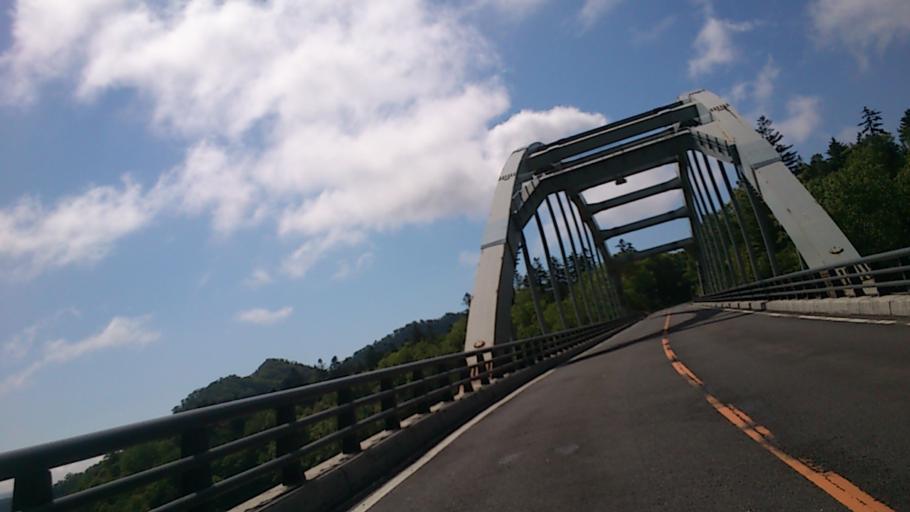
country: JP
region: Hokkaido
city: Shiraoi
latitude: 42.7175
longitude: 141.2067
